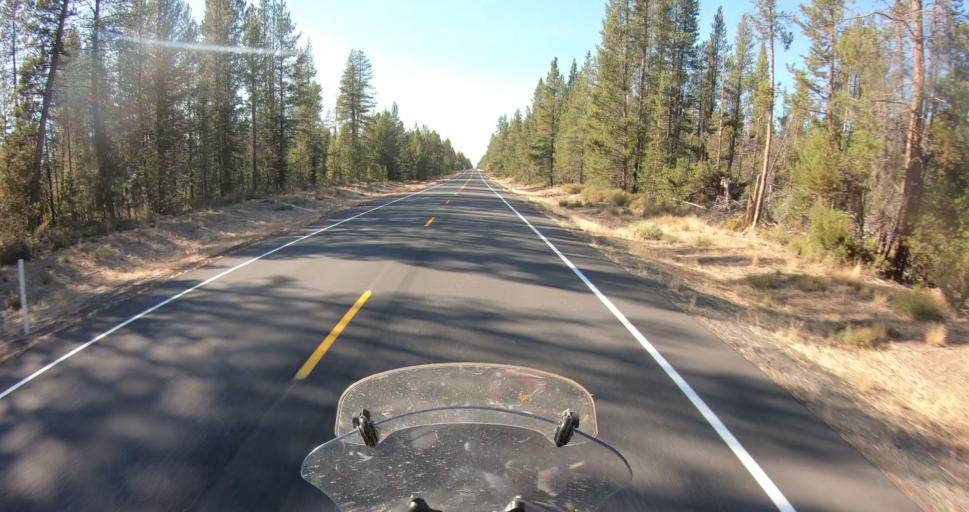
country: US
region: Oregon
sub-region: Deschutes County
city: La Pine
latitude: 43.4771
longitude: -121.4105
